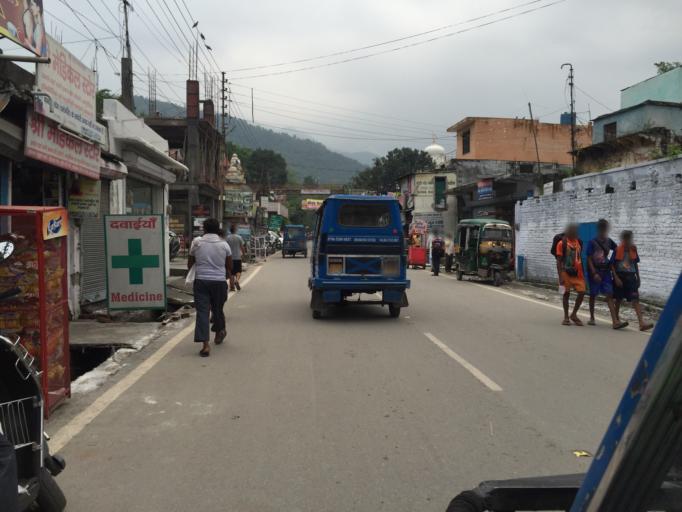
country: IN
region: Uttarakhand
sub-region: Dehradun
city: Rishikesh
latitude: 30.1165
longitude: 78.3035
